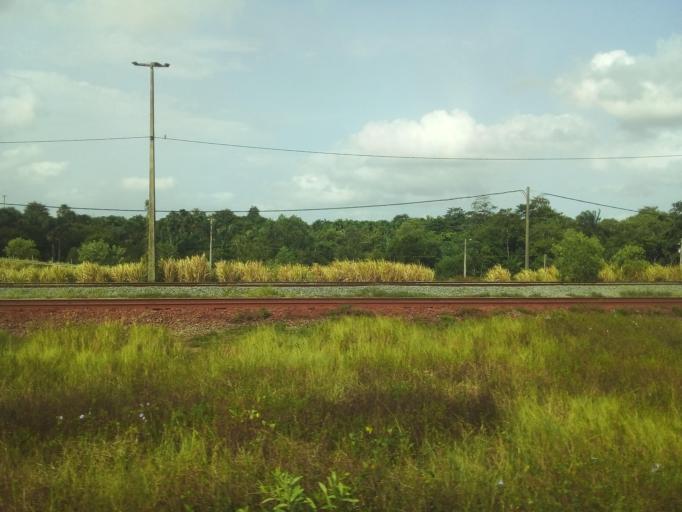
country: BR
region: Maranhao
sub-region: Sao Luis
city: Sao Luis
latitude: -2.6191
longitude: -44.3115
